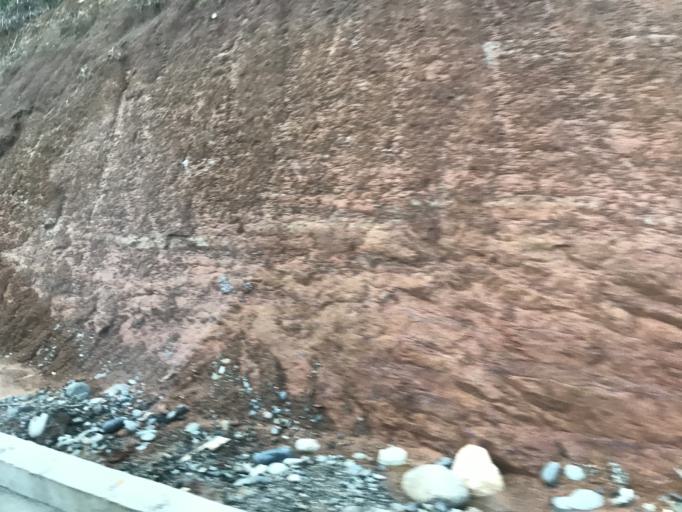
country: EC
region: Napo
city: Tena
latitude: -1.0648
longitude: -77.7011
